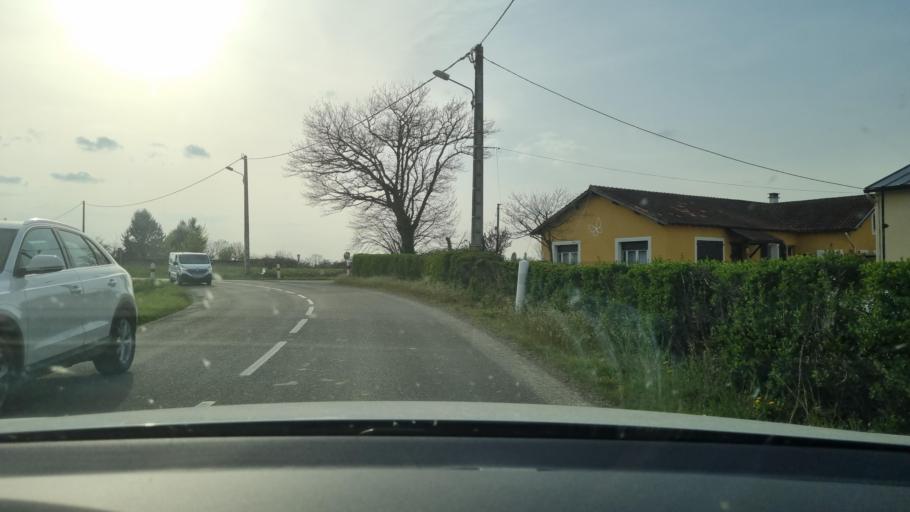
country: FR
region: Aquitaine
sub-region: Departement des Pyrenees-Atlantiques
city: Morlaas
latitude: 43.3641
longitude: -0.2114
